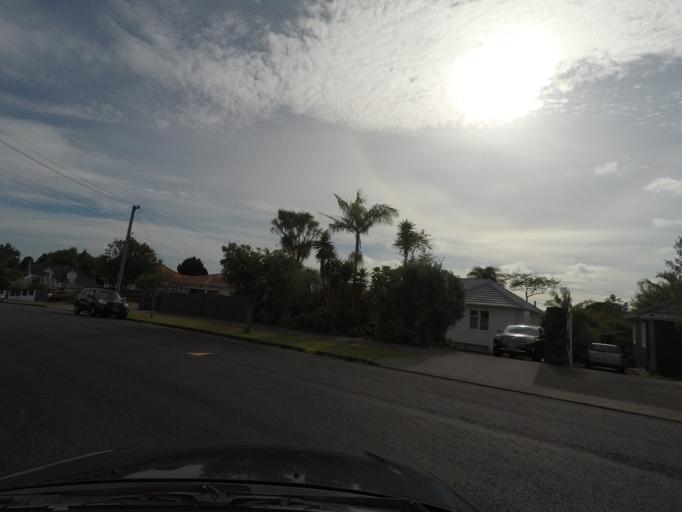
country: NZ
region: Auckland
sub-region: Auckland
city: Rosebank
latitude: -36.8767
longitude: 174.7160
